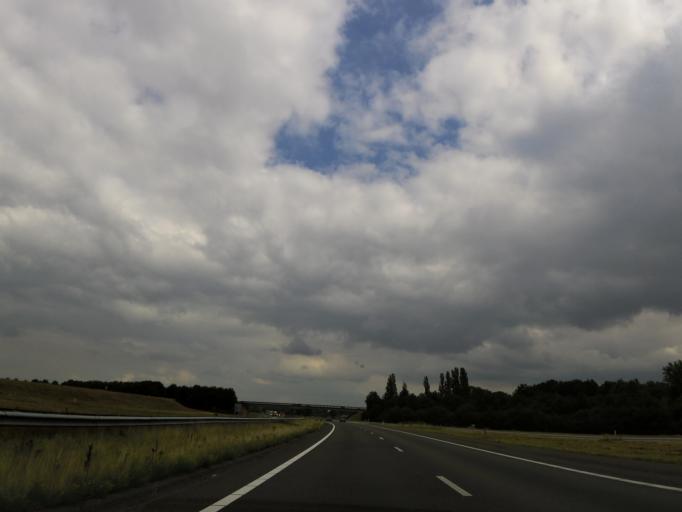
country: NL
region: Limburg
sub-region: Gemeente Weert
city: Weert
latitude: 51.2764
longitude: 5.6680
